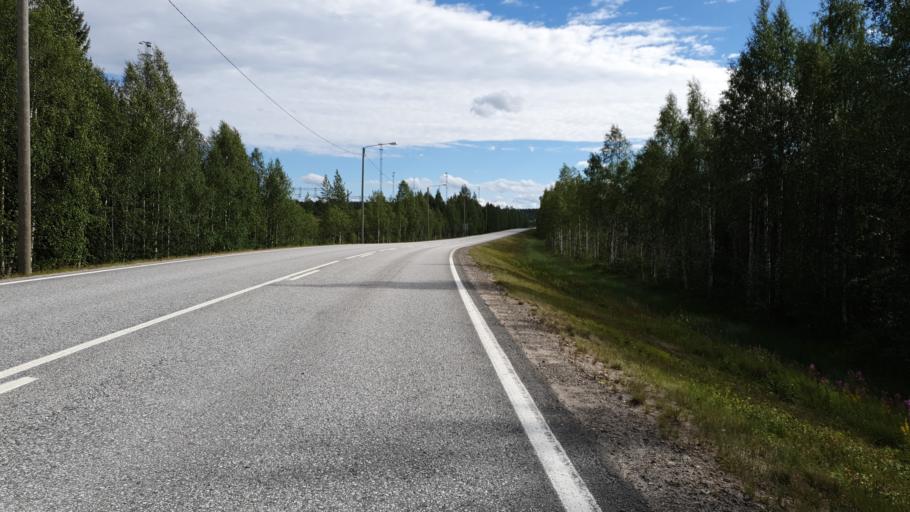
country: FI
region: Kainuu
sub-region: Kehys-Kainuu
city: Kuhmo
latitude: 64.5398
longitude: 29.9507
